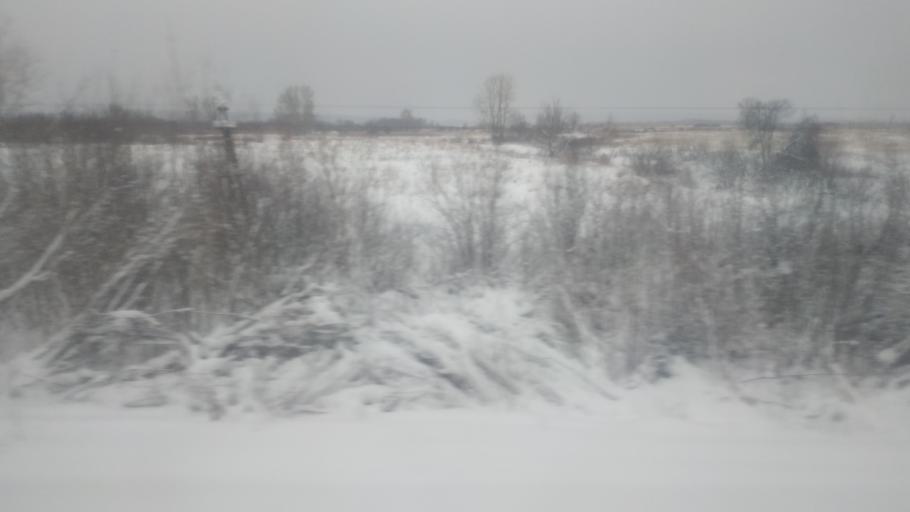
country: RU
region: Bashkortostan
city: Yanaul
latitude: 56.2502
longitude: 54.6729
